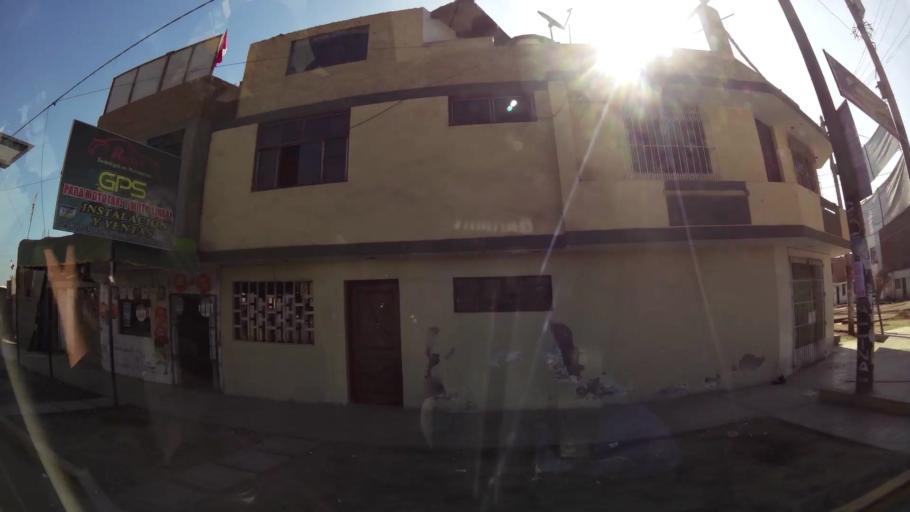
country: PE
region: Ica
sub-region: Provincia de Chincha
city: Chincha Alta
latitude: -13.4091
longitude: -76.1310
